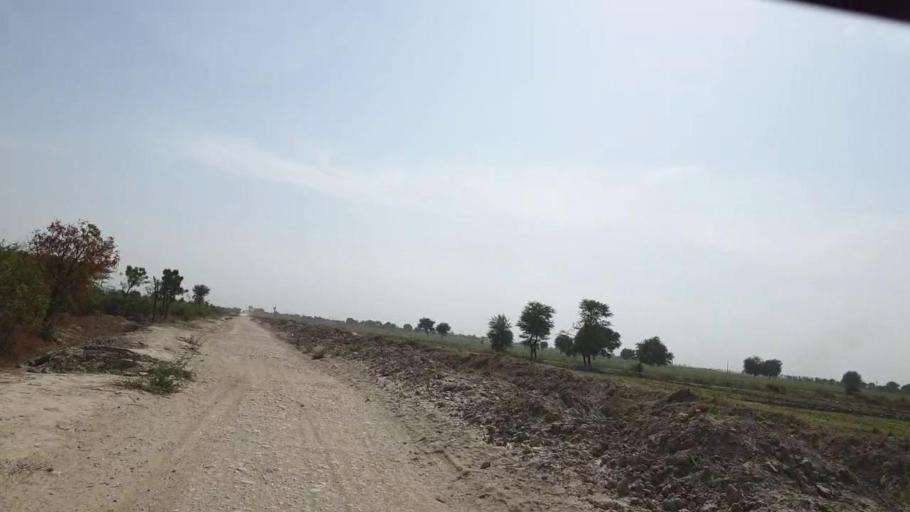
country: PK
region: Sindh
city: Nabisar
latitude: 25.0880
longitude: 69.5809
